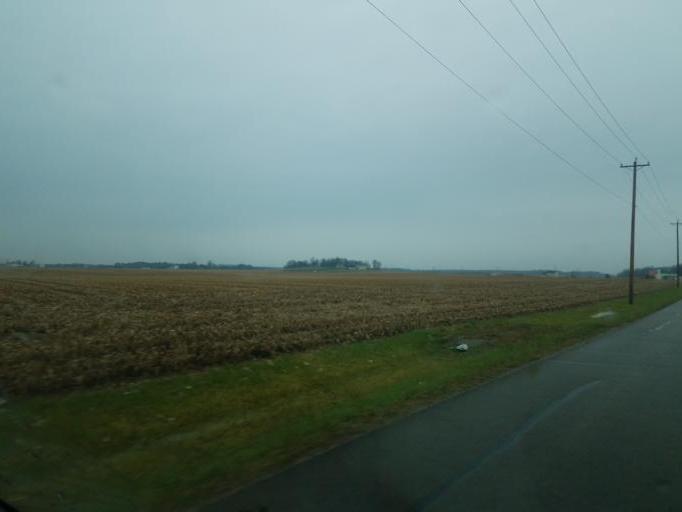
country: US
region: Ohio
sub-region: Knox County
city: Centerburg
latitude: 40.2528
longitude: -82.7162
